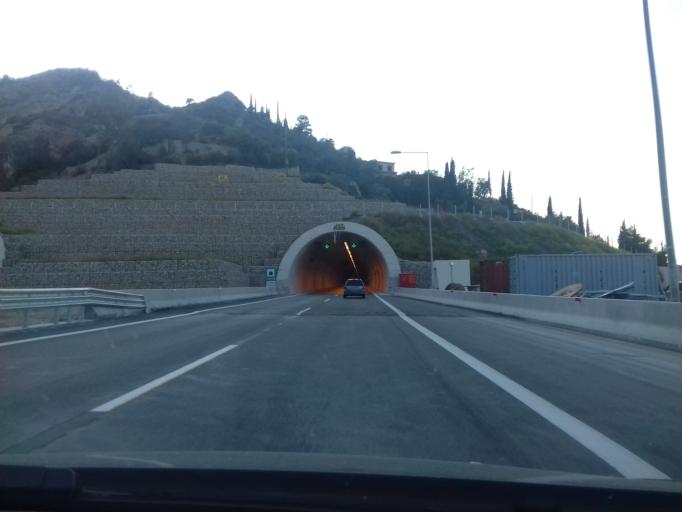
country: GR
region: West Greece
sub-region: Nomos Achaias
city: Aiyira
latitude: 38.1349
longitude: 22.3896
